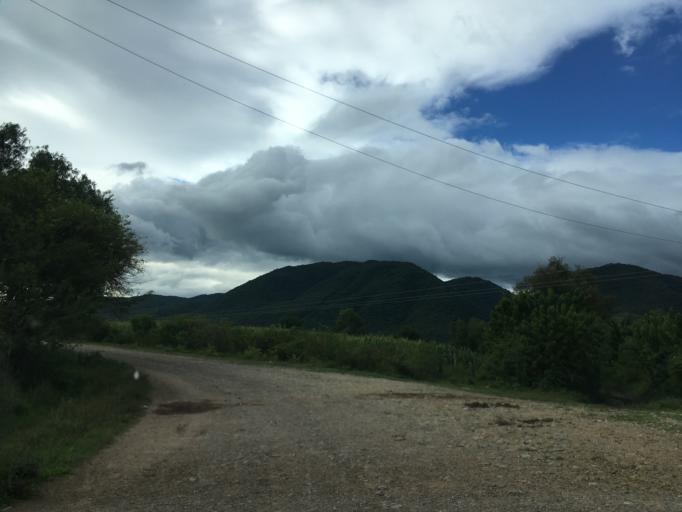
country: MX
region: Guanajuato
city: Iramuco
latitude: 19.9702
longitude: -100.9482
